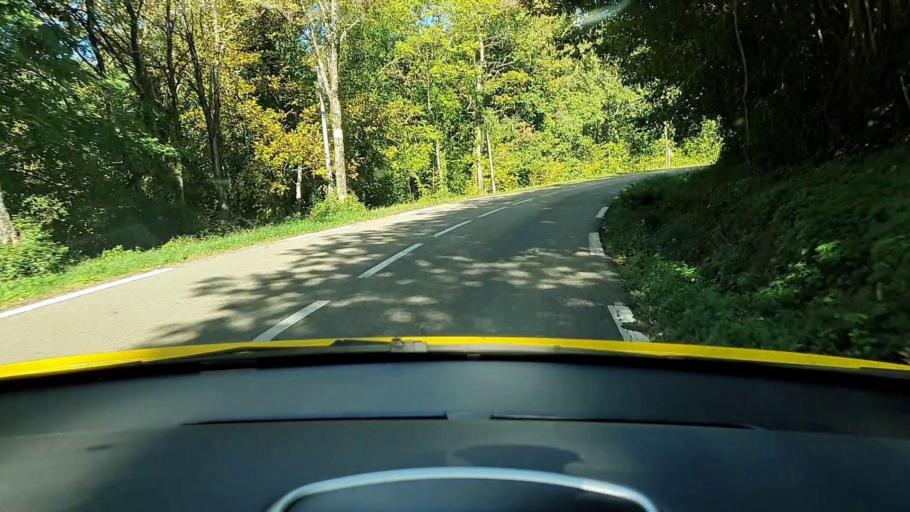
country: FR
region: Languedoc-Roussillon
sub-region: Departement du Gard
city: Le Vigan
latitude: 43.9675
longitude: 3.4177
